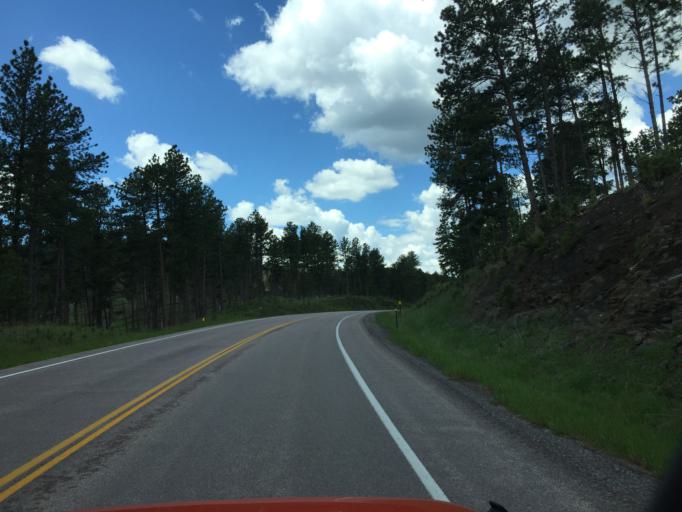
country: US
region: South Dakota
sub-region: Custer County
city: Custer
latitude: 43.8973
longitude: -103.5447
